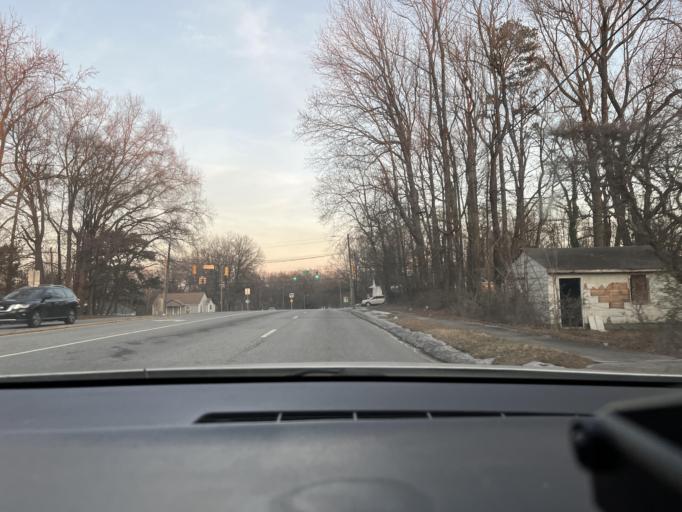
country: US
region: North Carolina
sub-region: Guilford County
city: Greensboro
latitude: 36.0628
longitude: -79.7625
